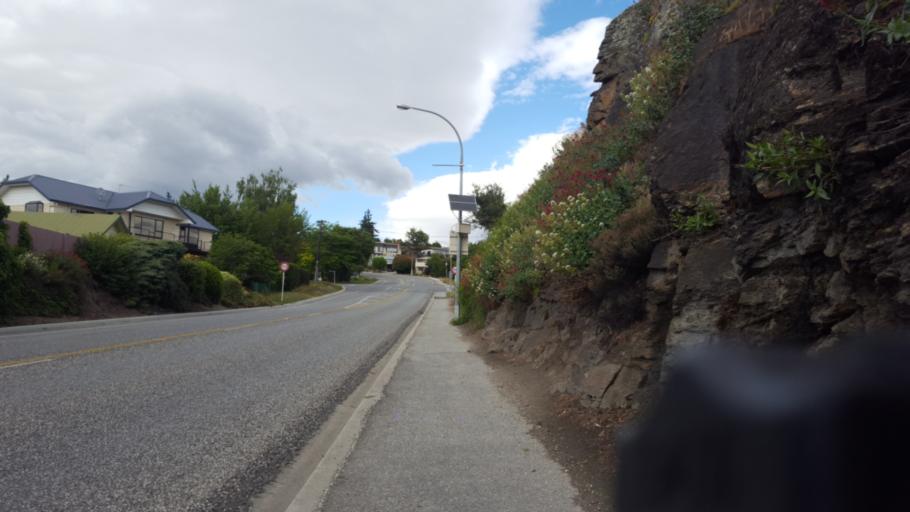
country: NZ
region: Otago
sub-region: Queenstown-Lakes District
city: Wanaka
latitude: -45.2600
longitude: 169.3891
